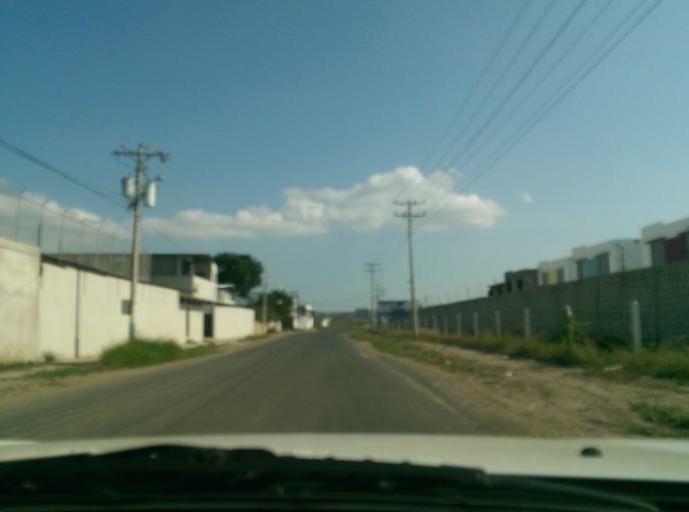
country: EC
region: Manabi
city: Manta
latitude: -0.9603
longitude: -80.7589
